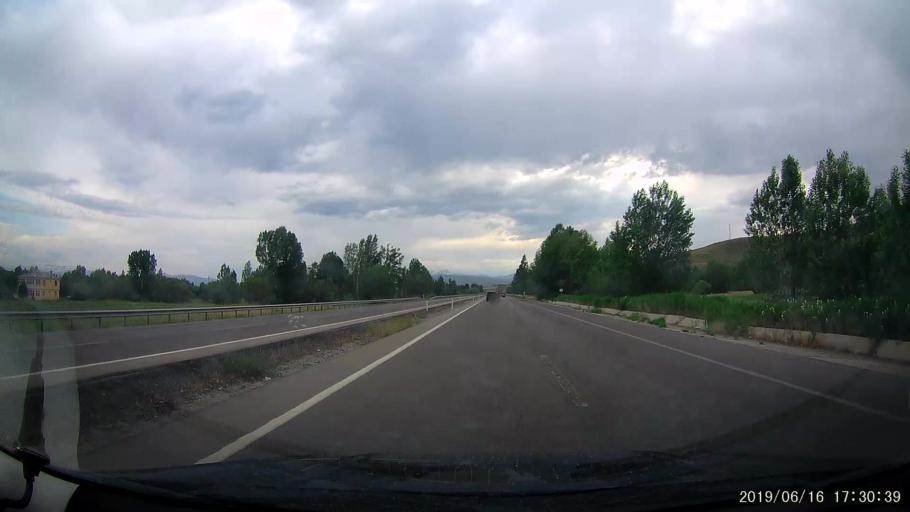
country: TR
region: Erzincan
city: Tercan
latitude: 39.7758
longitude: 40.3419
